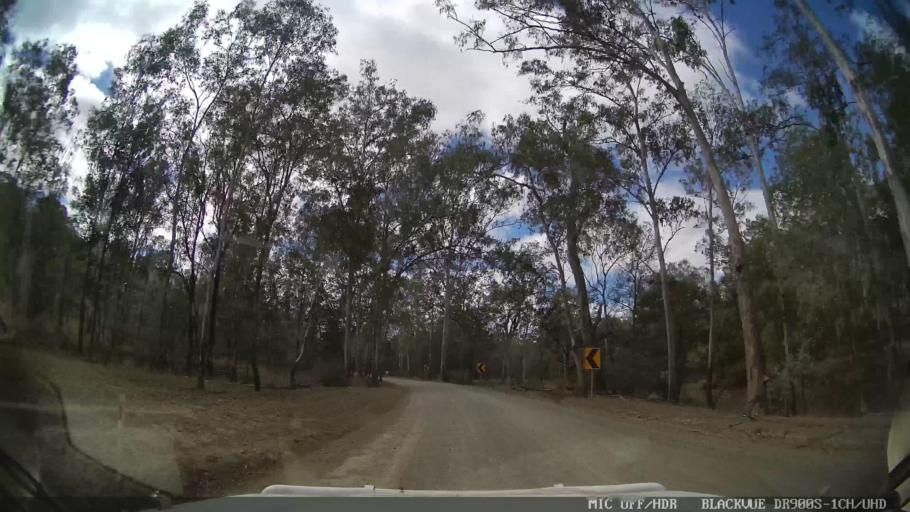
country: AU
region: Queensland
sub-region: Gladstone
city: Toolooa
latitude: -24.5507
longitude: 151.3407
